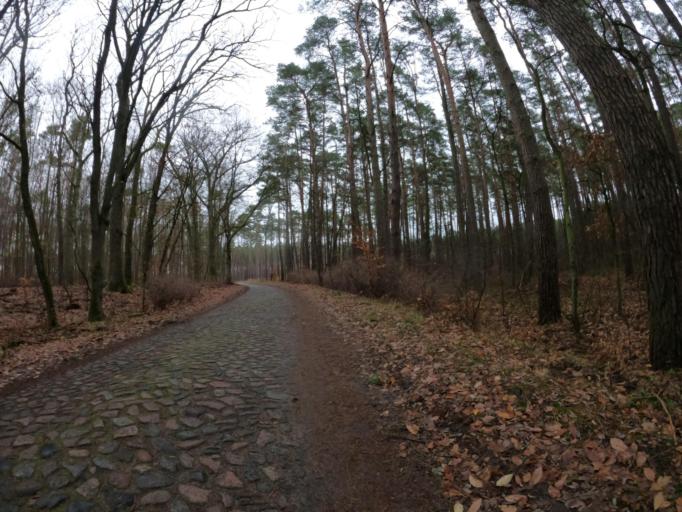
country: PL
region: West Pomeranian Voivodeship
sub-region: Powiat mysliborski
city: Debno
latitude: 52.7152
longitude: 14.7263
